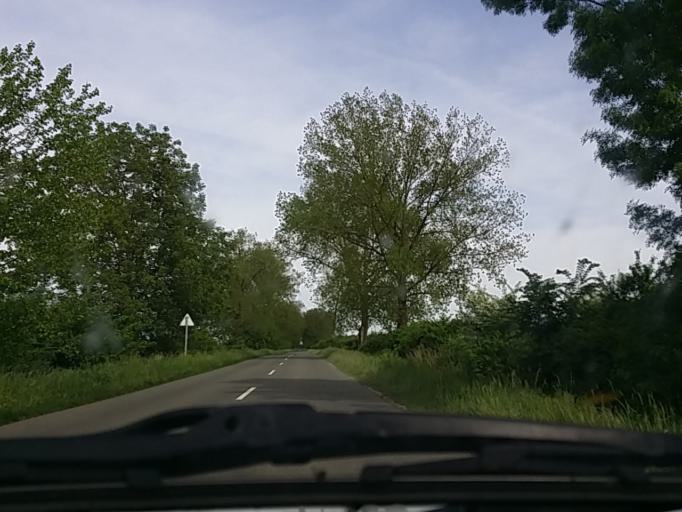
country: HU
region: Baranya
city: Vajszlo
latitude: 45.8420
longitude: 18.0659
